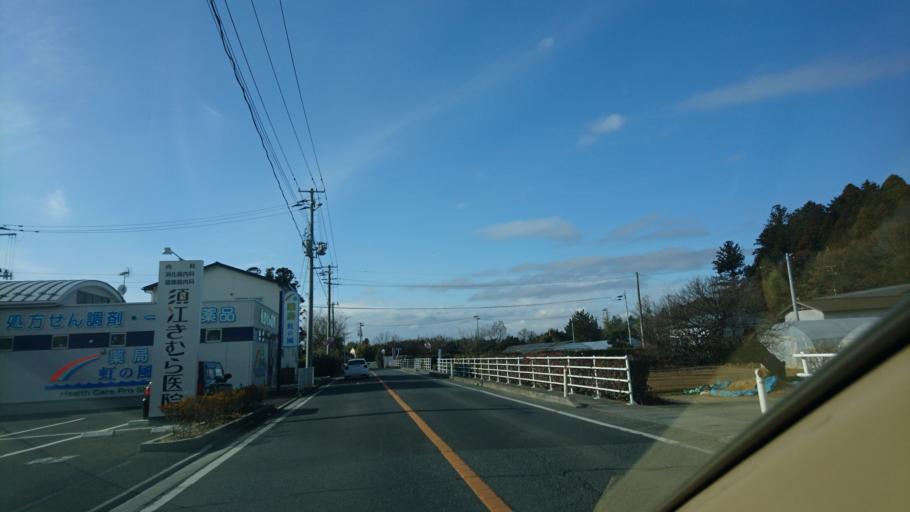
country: JP
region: Miyagi
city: Yamoto
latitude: 38.4571
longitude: 141.2532
